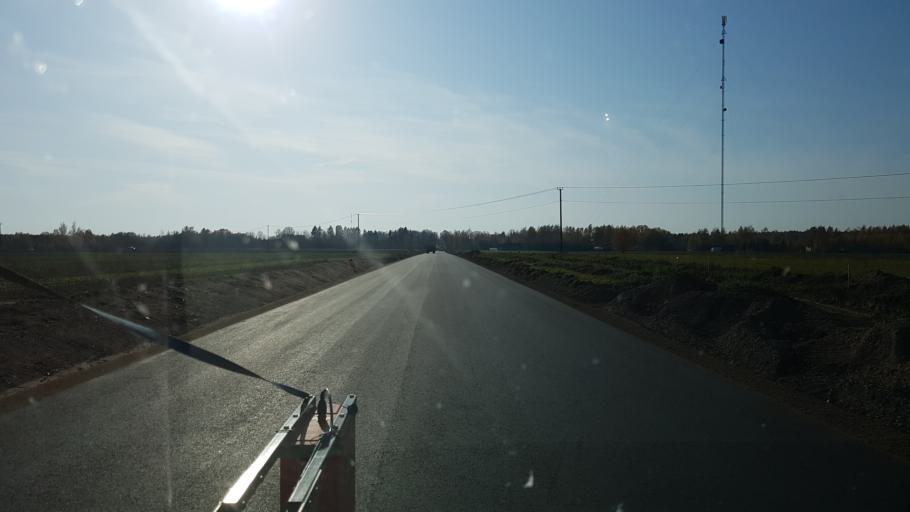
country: EE
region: Vorumaa
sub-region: Antsla vald
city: Vana-Antsla
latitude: 57.8389
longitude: 26.5476
